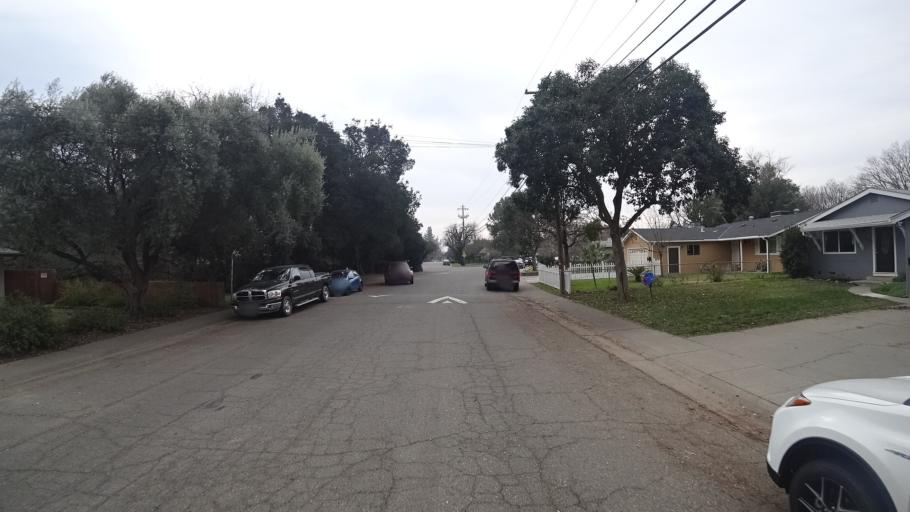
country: US
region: California
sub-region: Yolo County
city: Davis
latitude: 38.5598
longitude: -121.7278
